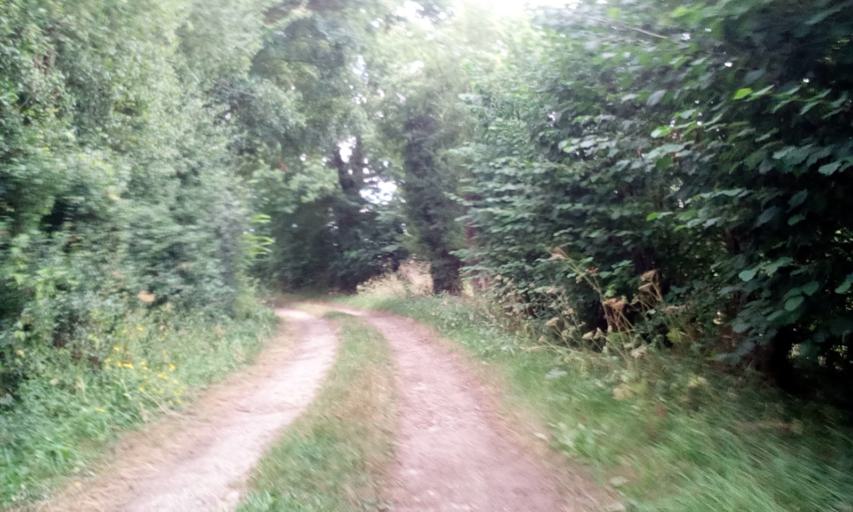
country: FR
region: Lower Normandy
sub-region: Departement du Calvados
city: Troarn
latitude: 49.1641
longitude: -0.1889
